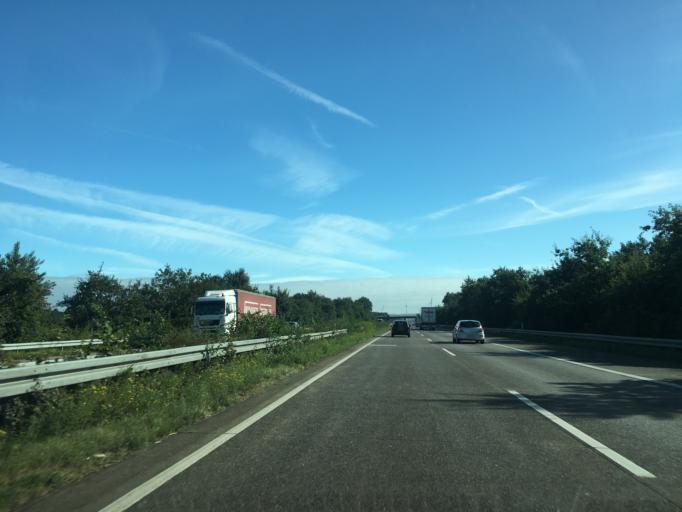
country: DE
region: North Rhine-Westphalia
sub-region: Regierungsbezirk Munster
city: Ladbergen
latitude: 52.1663
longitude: 7.7555
